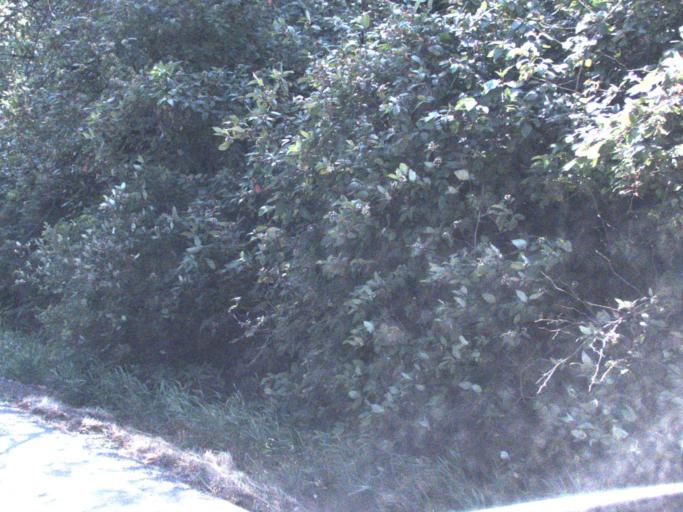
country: US
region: Washington
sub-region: King County
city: Sammamish
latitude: 47.6549
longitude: -122.0572
